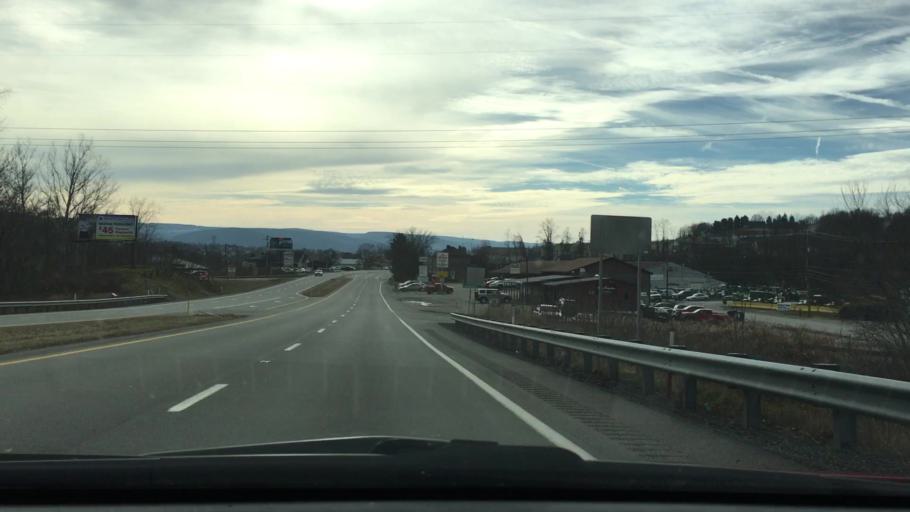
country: US
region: Pennsylvania
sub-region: Fayette County
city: Oliver
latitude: 39.9292
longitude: -79.7281
